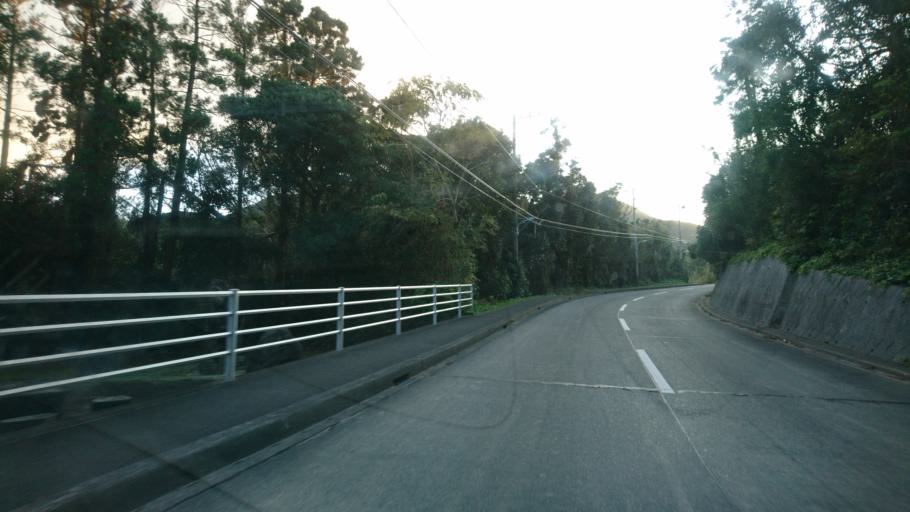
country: JP
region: Shizuoka
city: Shimoda
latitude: 34.3651
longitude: 139.2586
